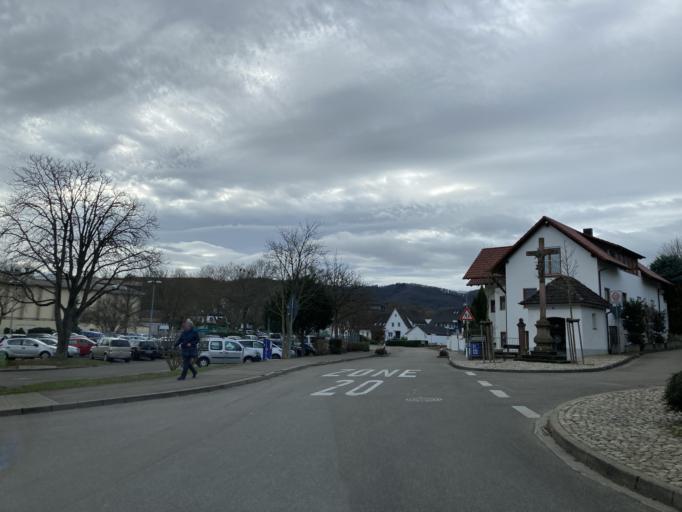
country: DE
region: Baden-Wuerttemberg
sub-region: Freiburg Region
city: Endingen
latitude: 48.1387
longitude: 7.7033
